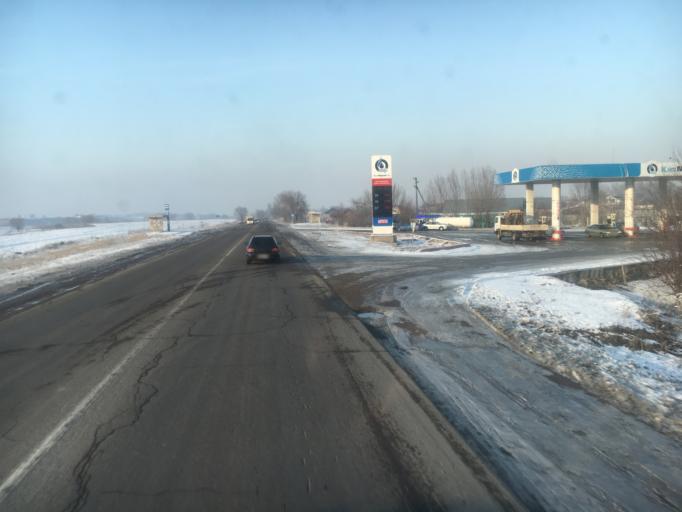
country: KZ
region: Almaty Oblysy
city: Burunday
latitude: 43.2896
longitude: 76.6734
